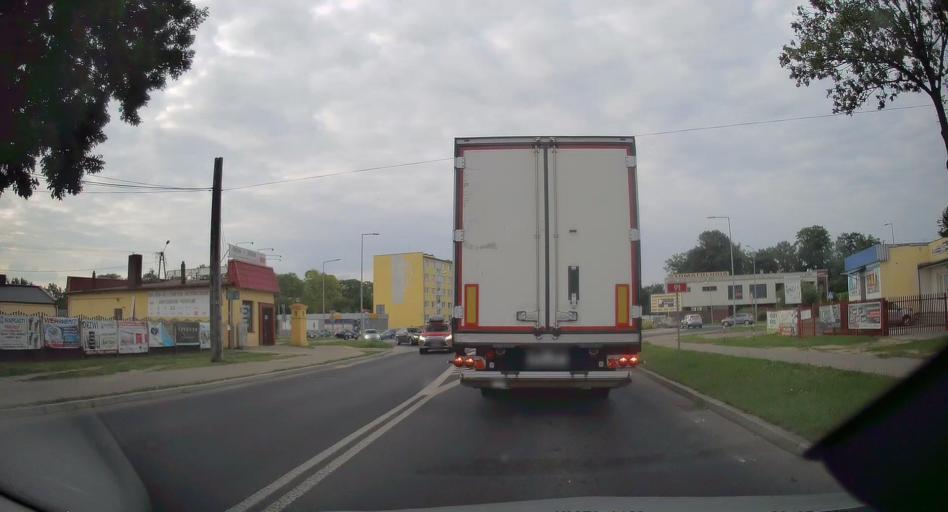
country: PL
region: Lodz Voivodeship
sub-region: Powiat radomszczanski
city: Radomsko
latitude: 51.0616
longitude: 19.4419
